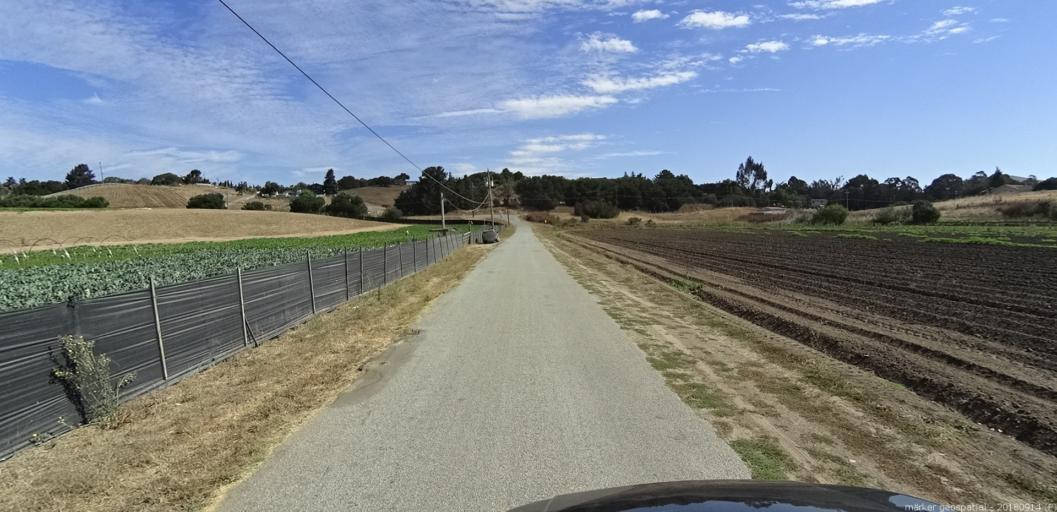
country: US
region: California
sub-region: San Benito County
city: Aromas
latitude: 36.8568
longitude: -121.6482
